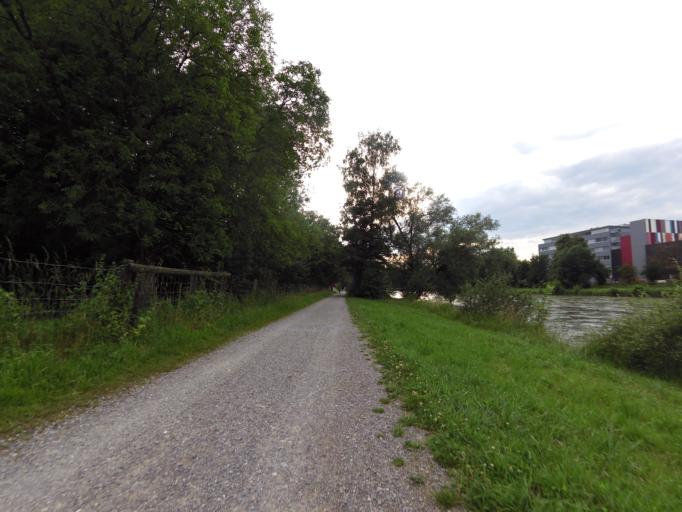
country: CH
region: Zurich
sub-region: Bezirk Dietikon
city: Dietikon / Schoenenwerd
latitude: 47.3997
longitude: 8.4259
